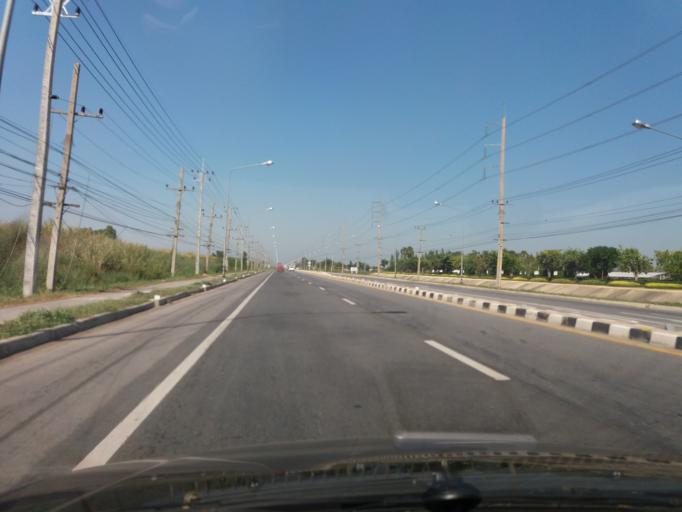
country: TH
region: Chai Nat
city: Manorom
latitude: 15.2792
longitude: 100.0955
